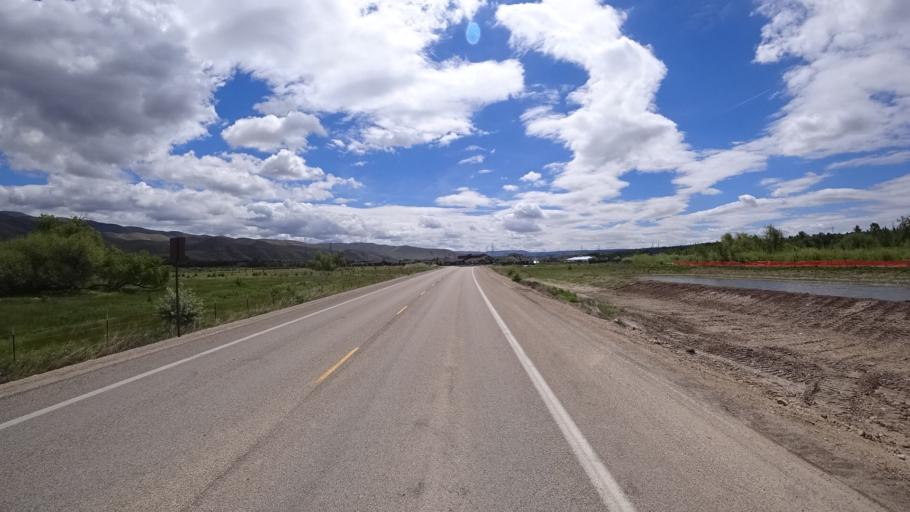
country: US
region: Idaho
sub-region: Ada County
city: Boise
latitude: 43.5705
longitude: -116.1334
